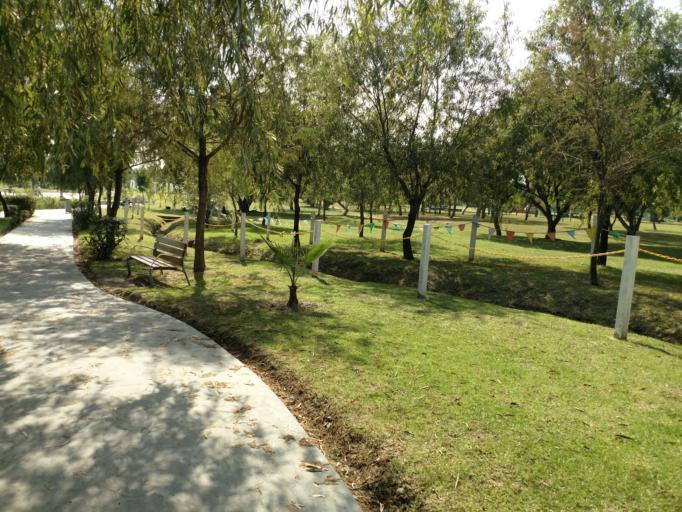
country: MX
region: Jalisco
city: Guadalajara
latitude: 20.6742
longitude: -103.4405
